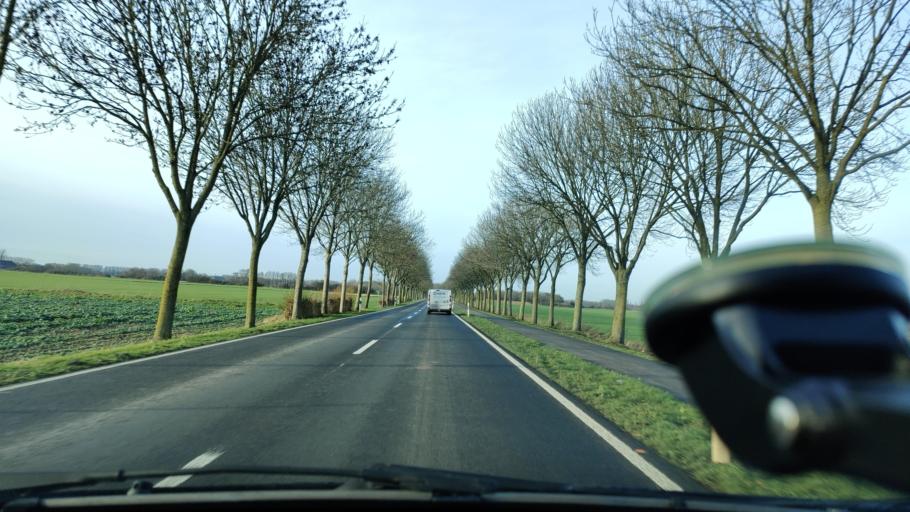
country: DE
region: North Rhine-Westphalia
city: Kalkar
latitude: 51.7475
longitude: 6.3214
